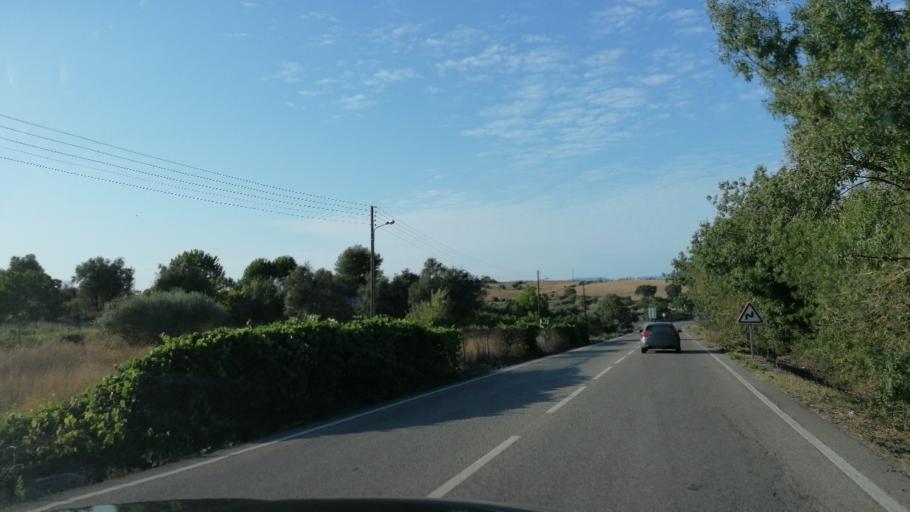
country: PT
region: Santarem
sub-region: Santarem
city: Santarem
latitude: 39.3165
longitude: -8.6702
